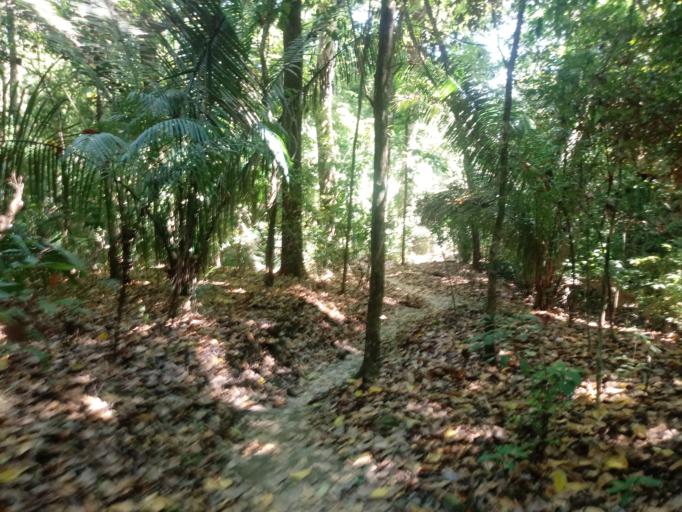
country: CR
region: Puntarenas
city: Paquera
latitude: 9.5857
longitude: -85.0954
